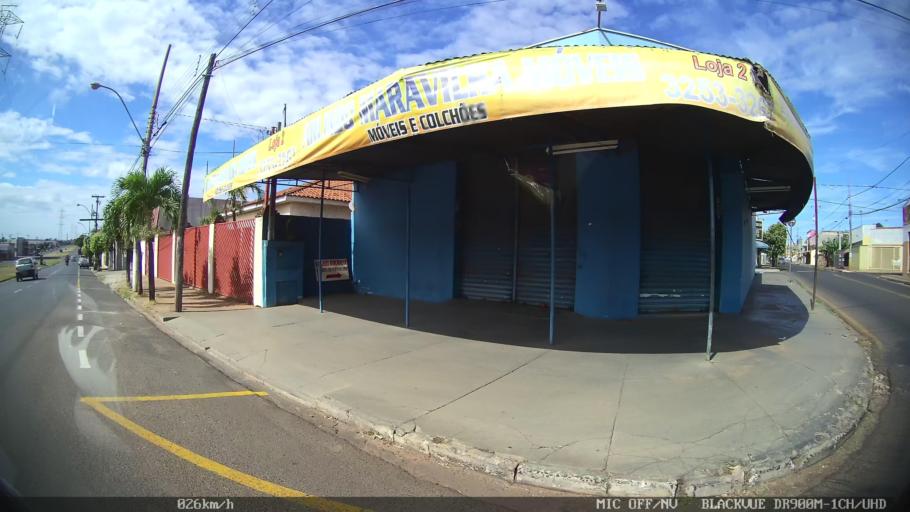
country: BR
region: Sao Paulo
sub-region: Bady Bassitt
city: Bady Bassitt
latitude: -20.8126
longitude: -49.5179
